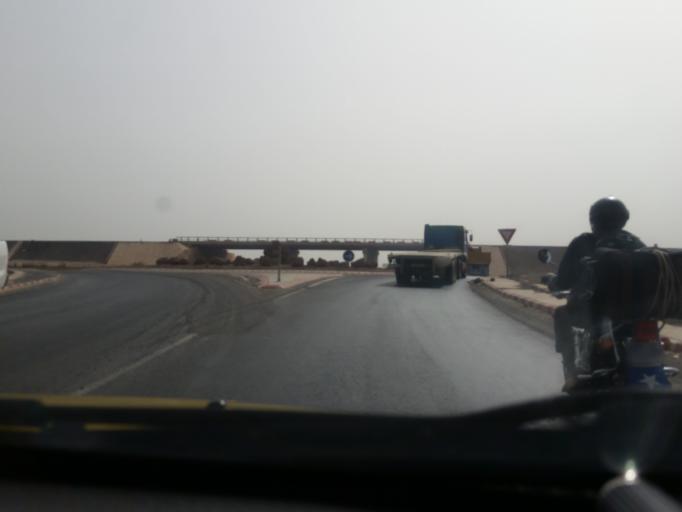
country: SN
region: Thies
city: Pout
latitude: 14.7308
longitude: -17.1610
